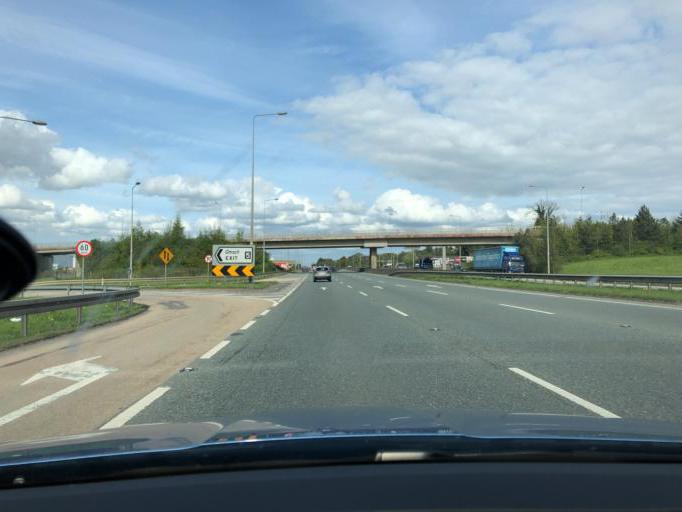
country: IE
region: Leinster
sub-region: South Dublin
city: Newcastle
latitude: 53.2683
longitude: -6.5221
